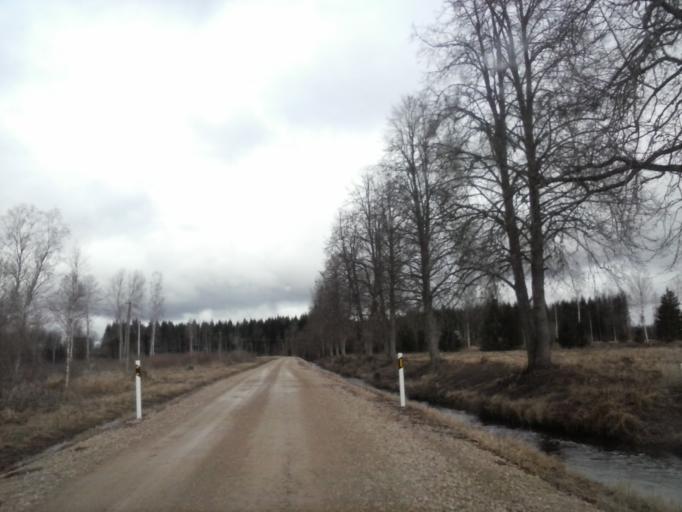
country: EE
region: Jogevamaa
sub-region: Mustvee linn
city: Mustvee
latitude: 59.0916
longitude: 26.8627
